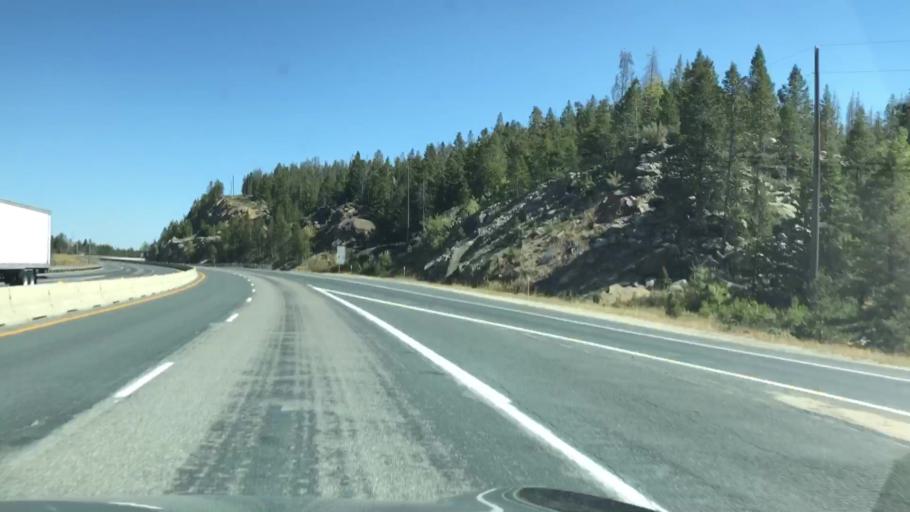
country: US
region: Montana
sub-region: Silver Bow County
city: Butte
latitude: 45.9158
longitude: -112.3741
